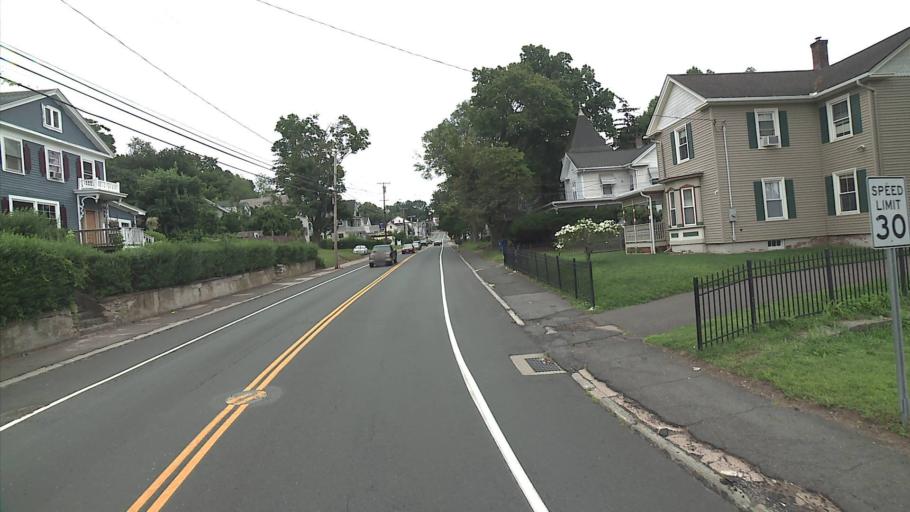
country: US
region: Connecticut
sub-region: Tolland County
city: Rockville
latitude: 41.8679
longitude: -72.4564
